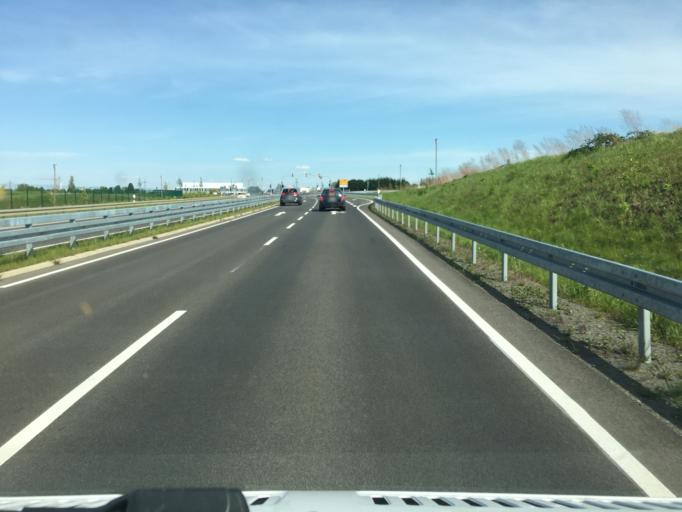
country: DE
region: North Rhine-Westphalia
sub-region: Regierungsbezirk Koln
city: Hurth
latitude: 50.8742
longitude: 6.8945
